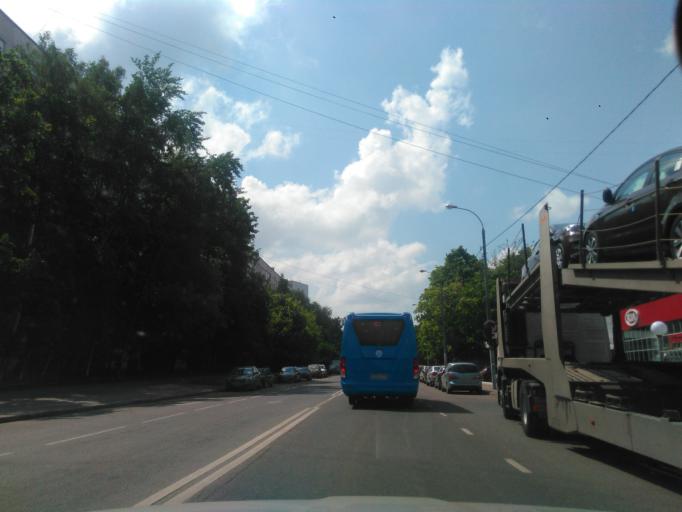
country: RU
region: Moscow
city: Zapadnoye Degunino
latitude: 55.8867
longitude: 37.5237
